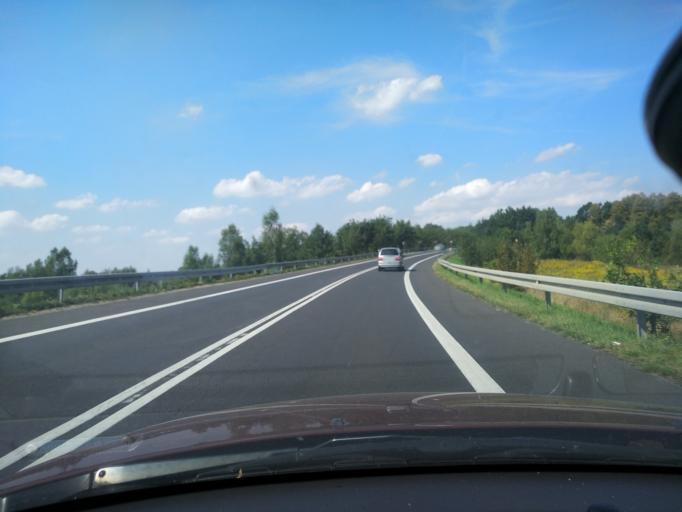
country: PL
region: Lower Silesian Voivodeship
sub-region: Powiat lubanski
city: Luban
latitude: 51.0851
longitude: 15.3229
